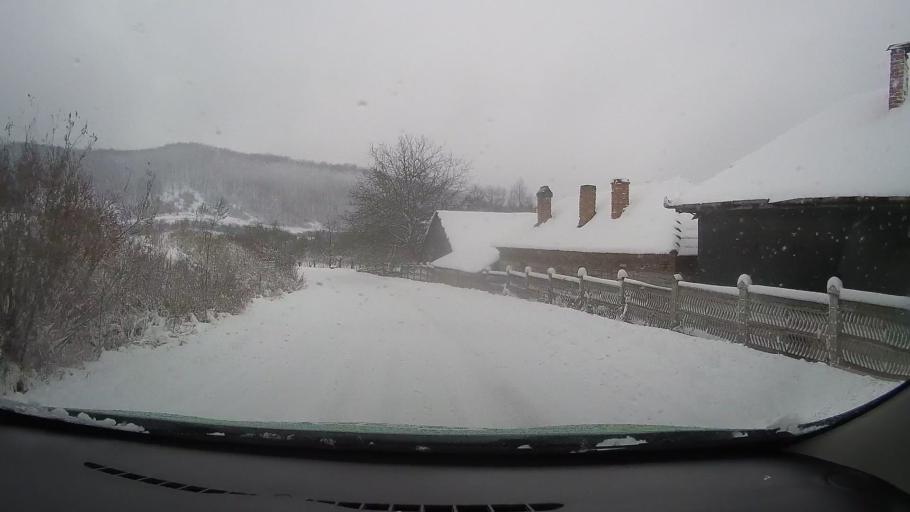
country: RO
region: Hunedoara
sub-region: Comuna Carjiti
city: Carjiti
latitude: 45.8433
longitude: 22.8300
